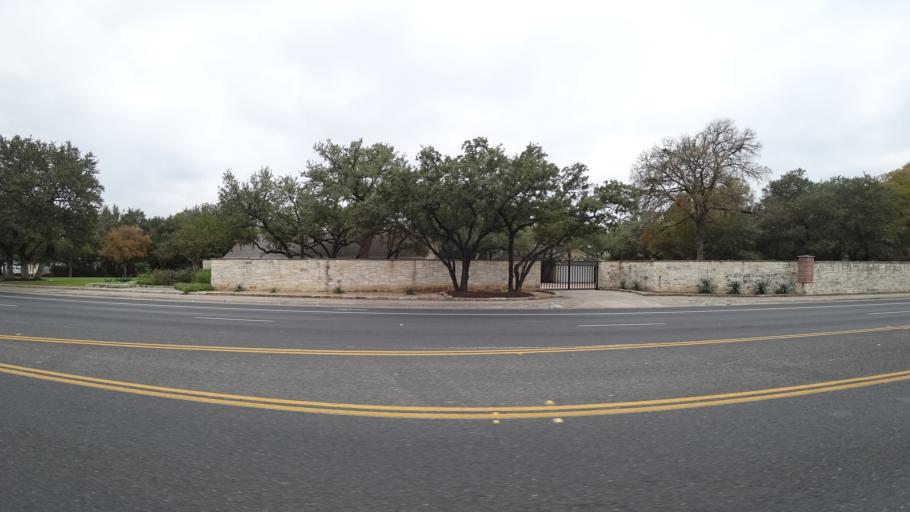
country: US
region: Texas
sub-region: Williamson County
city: Anderson Mill
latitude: 30.4499
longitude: -97.8168
